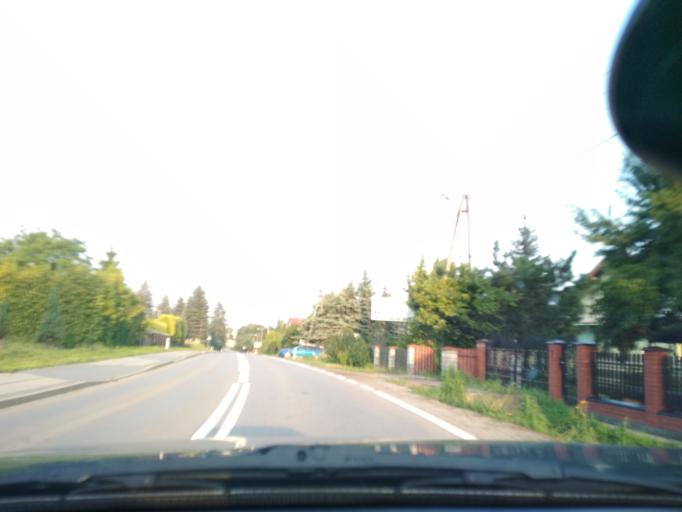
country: PL
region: Lesser Poland Voivodeship
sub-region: Powiat olkuski
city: Wolbrom
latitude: 50.3924
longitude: 19.7466
